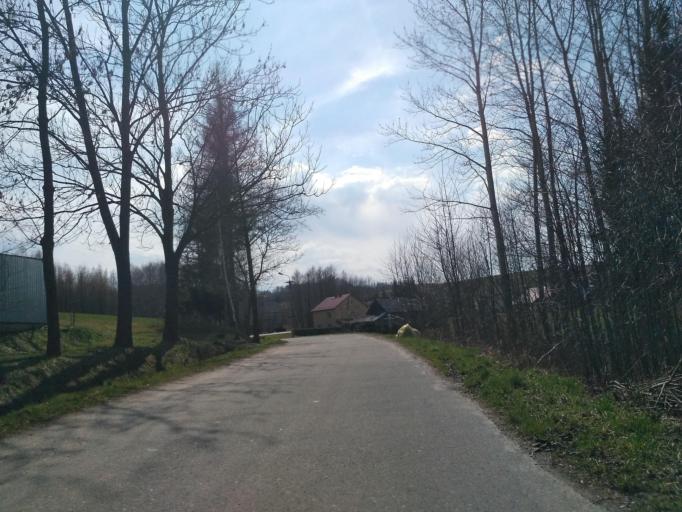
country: PL
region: Subcarpathian Voivodeship
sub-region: Powiat ropczycko-sedziszowski
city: Iwierzyce
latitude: 49.9996
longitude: 21.7556
